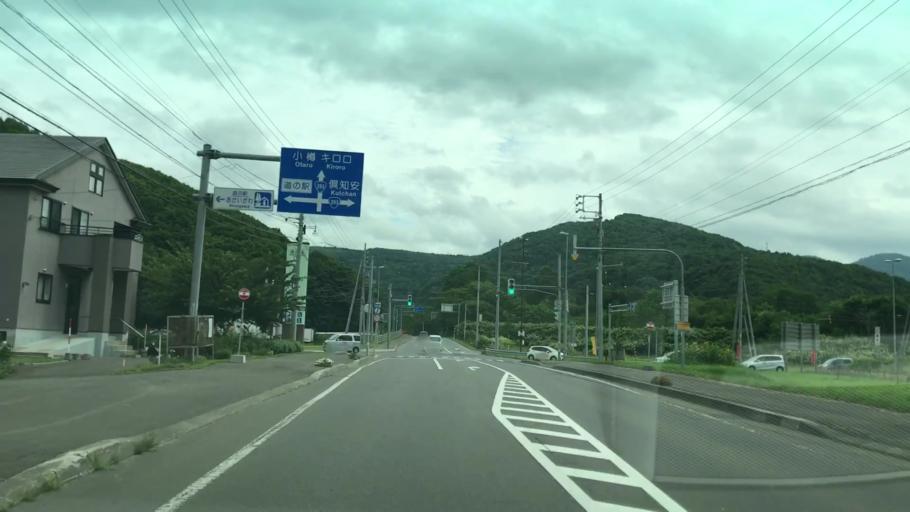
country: JP
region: Hokkaido
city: Yoichi
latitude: 43.0505
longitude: 140.8432
